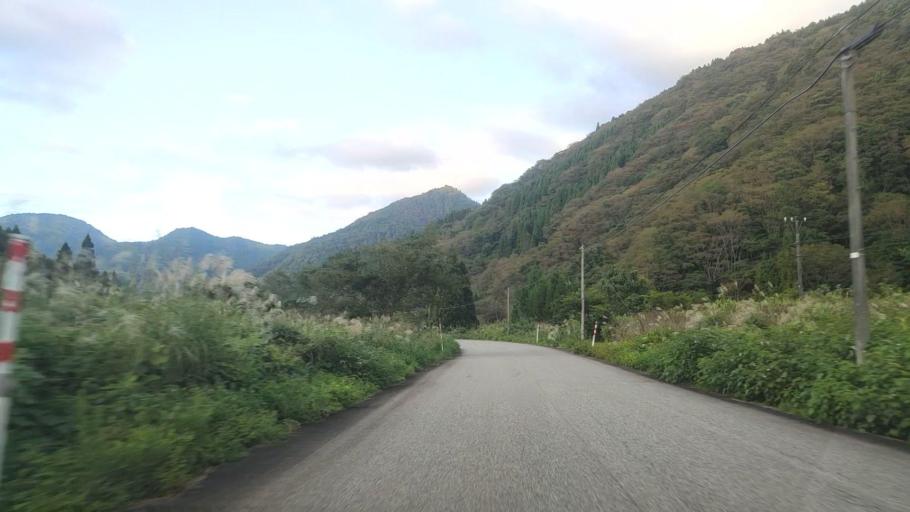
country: JP
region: Toyama
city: Yatsuomachi-higashikumisaka
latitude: 36.4652
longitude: 137.0856
